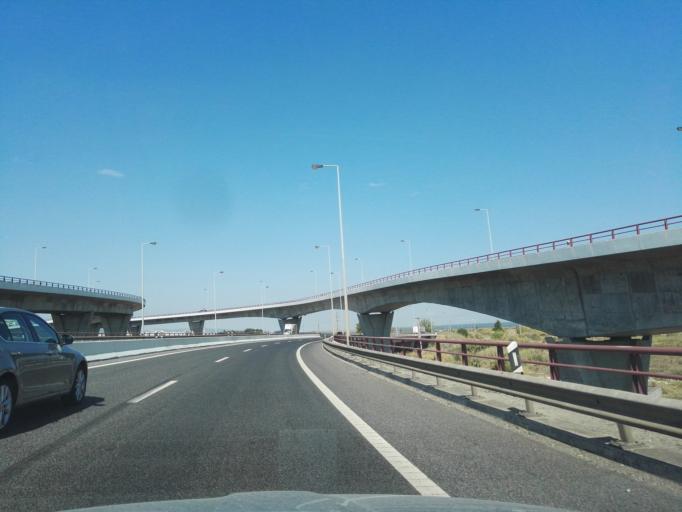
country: PT
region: Lisbon
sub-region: Loures
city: Sacavem
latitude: 38.7966
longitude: -9.0985
